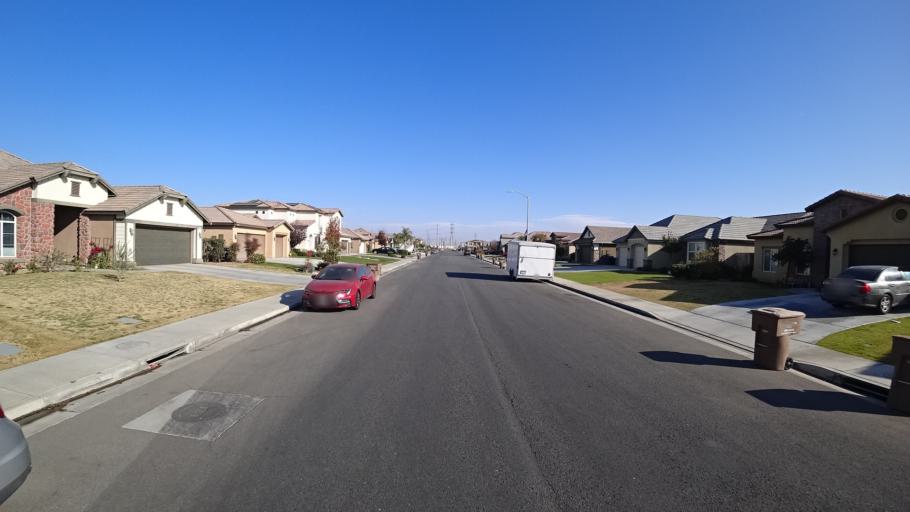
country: US
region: California
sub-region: Kern County
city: Greenacres
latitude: 35.3785
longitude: -119.1050
